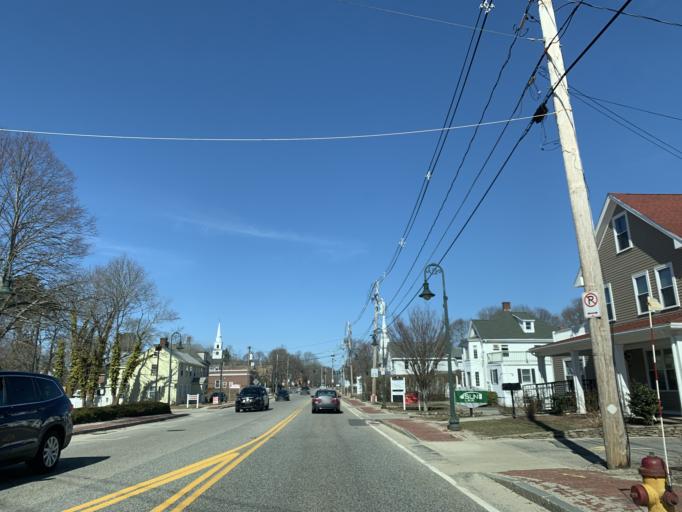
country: US
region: Massachusetts
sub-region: Norfolk County
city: Sharon
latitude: 42.1220
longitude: -71.1799
